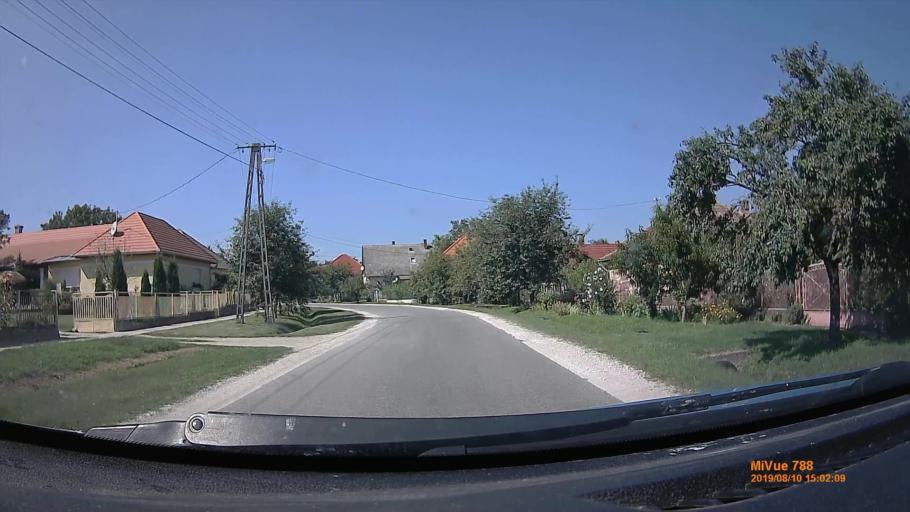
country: HU
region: Somogy
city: Lengyeltoti
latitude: 46.6540
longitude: 17.5765
